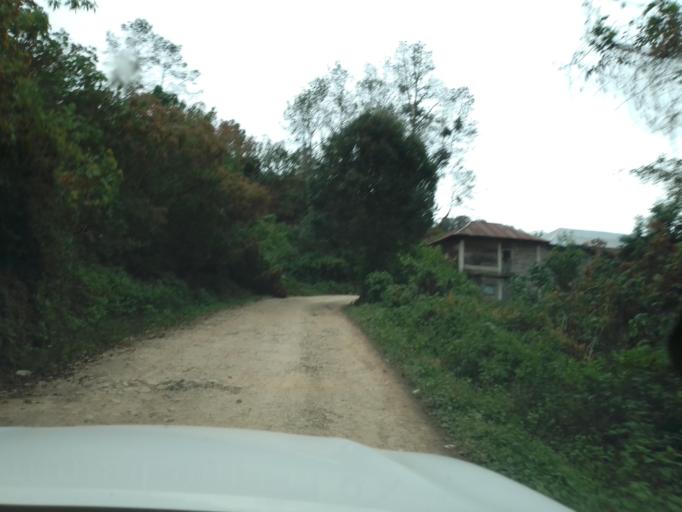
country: MX
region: Chiapas
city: Motozintla de Mendoza
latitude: 15.2206
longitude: -92.2279
